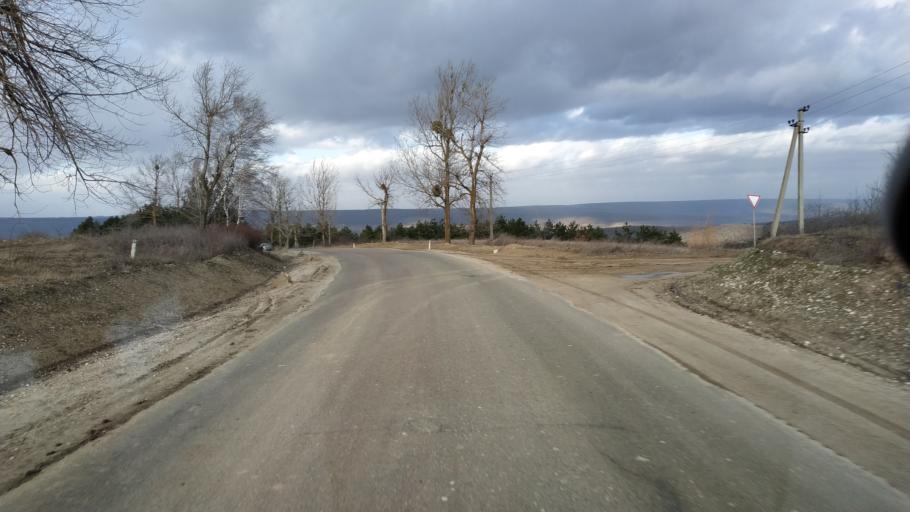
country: MD
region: Calarasi
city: Calarasi
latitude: 47.2886
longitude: 28.3587
